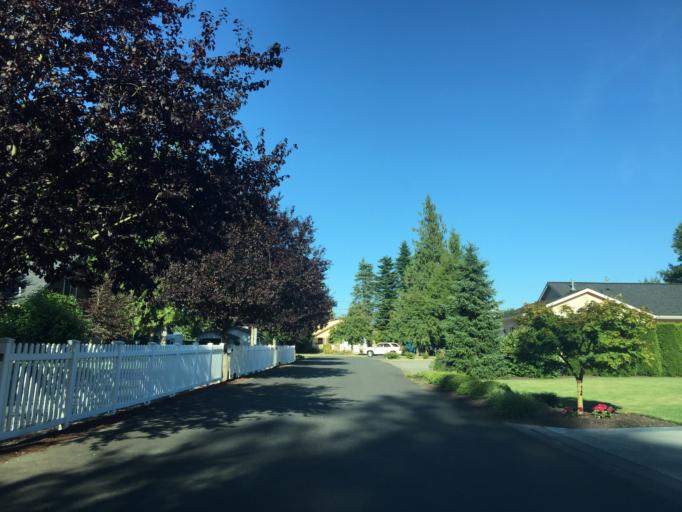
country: US
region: Washington
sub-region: Whatcom County
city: Lynden
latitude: 48.9450
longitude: -122.4756
